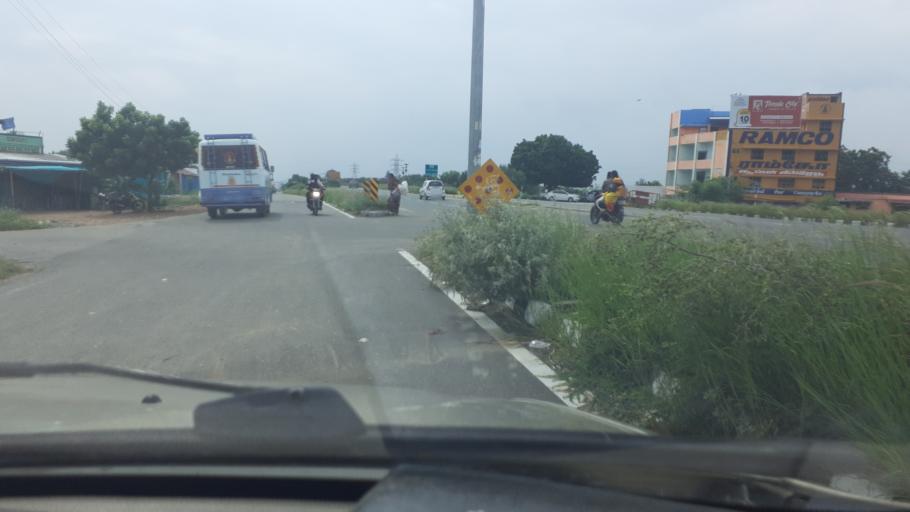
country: IN
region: Tamil Nadu
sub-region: Madurai
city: Tirupparangunram
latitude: 9.8371
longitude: 77.9857
